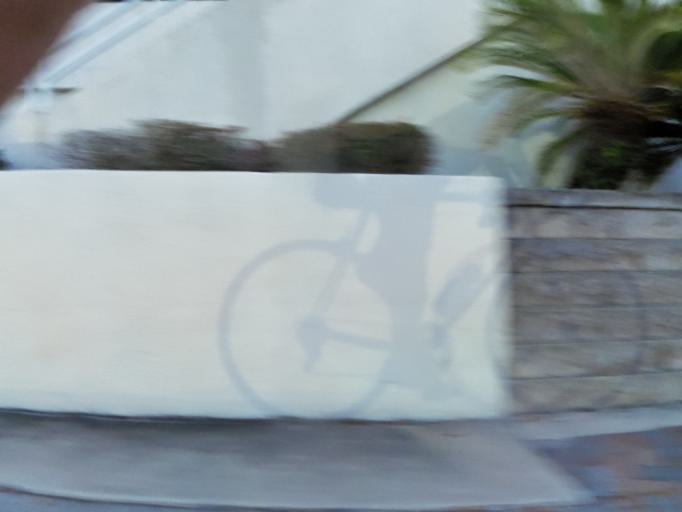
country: US
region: Florida
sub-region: Duval County
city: Jacksonville
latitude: 30.3250
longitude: -81.6770
